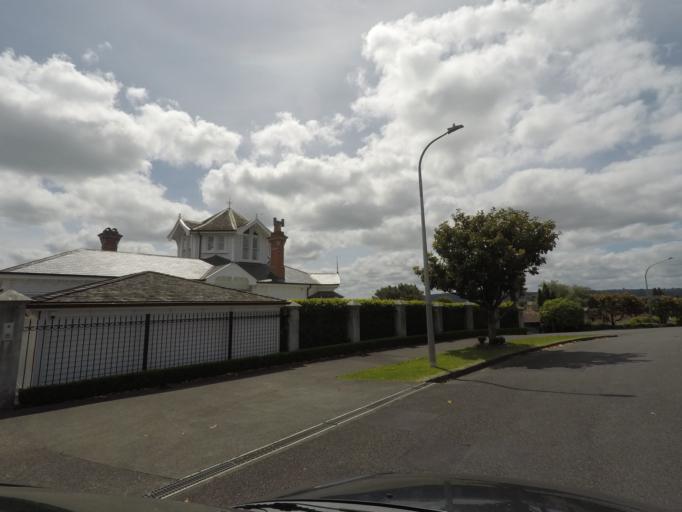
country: NZ
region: Auckland
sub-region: Auckland
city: Auckland
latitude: -36.8476
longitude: 174.7243
